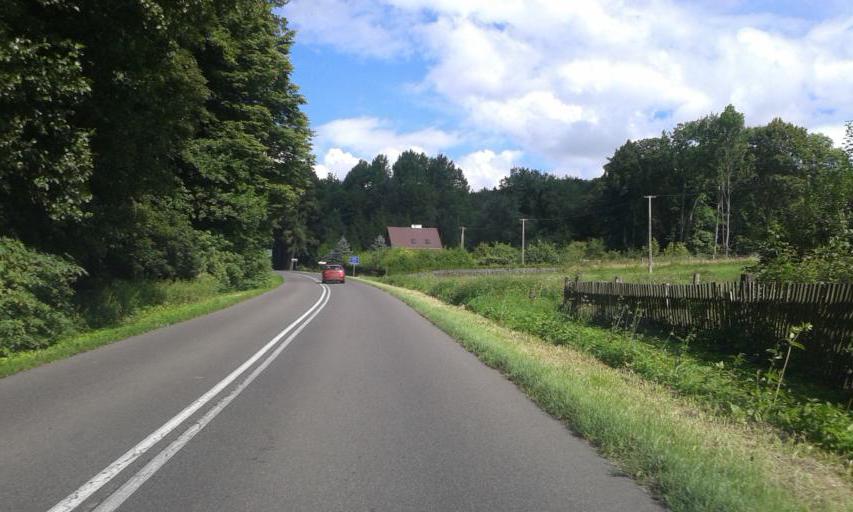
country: PL
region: West Pomeranian Voivodeship
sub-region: Powiat koszalinski
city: Polanow
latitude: 54.2170
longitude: 16.7014
